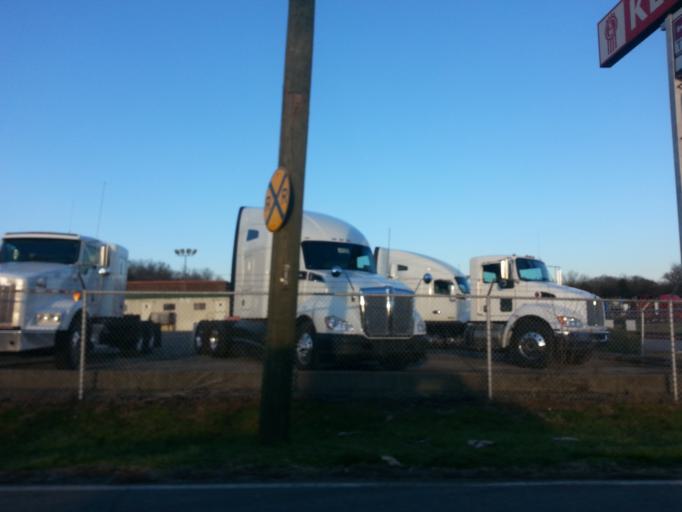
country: US
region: Tennessee
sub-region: Knox County
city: Knoxville
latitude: 36.0109
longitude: -83.8751
